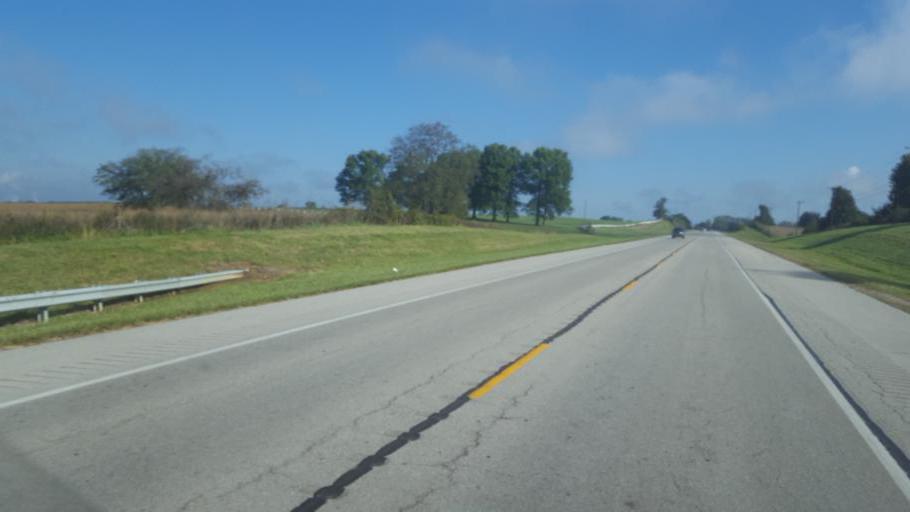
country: US
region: Kentucky
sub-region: Mason County
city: Maysville
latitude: 38.5839
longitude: -83.7745
